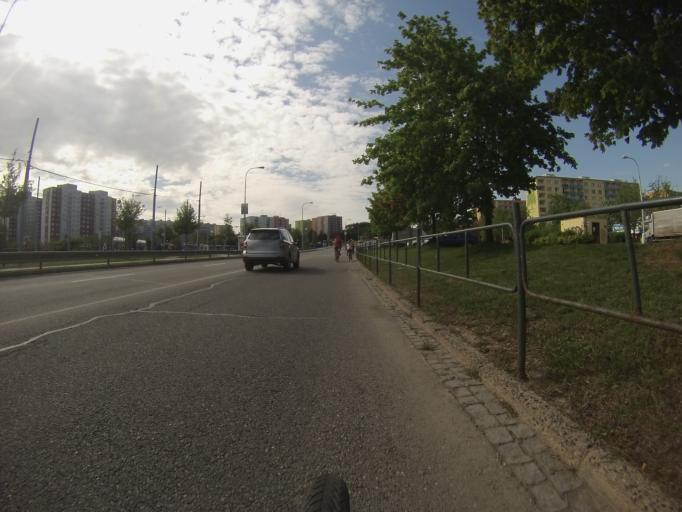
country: CZ
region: South Moravian
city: Troubsko
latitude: 49.2180
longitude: 16.5101
